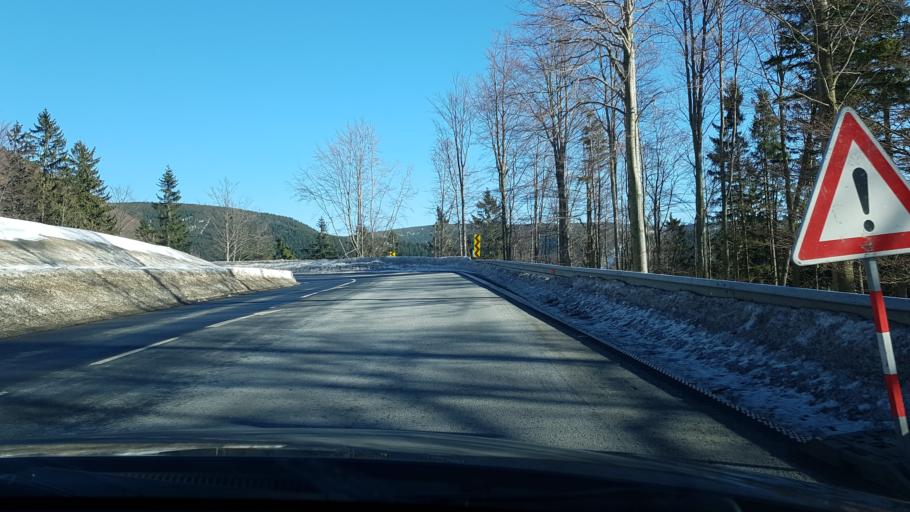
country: CZ
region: Olomoucky
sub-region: Okres Sumperk
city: Loucna nad Desnou
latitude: 50.1143
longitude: 17.1509
